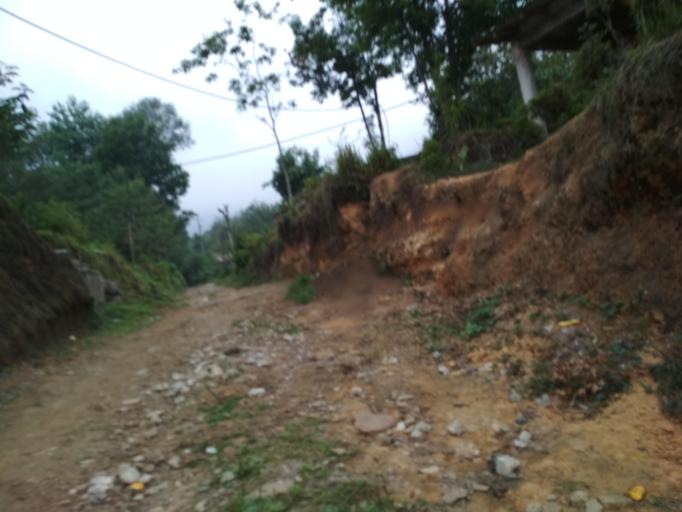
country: MX
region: Veracruz
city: La Perla
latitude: 18.9322
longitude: -97.1419
